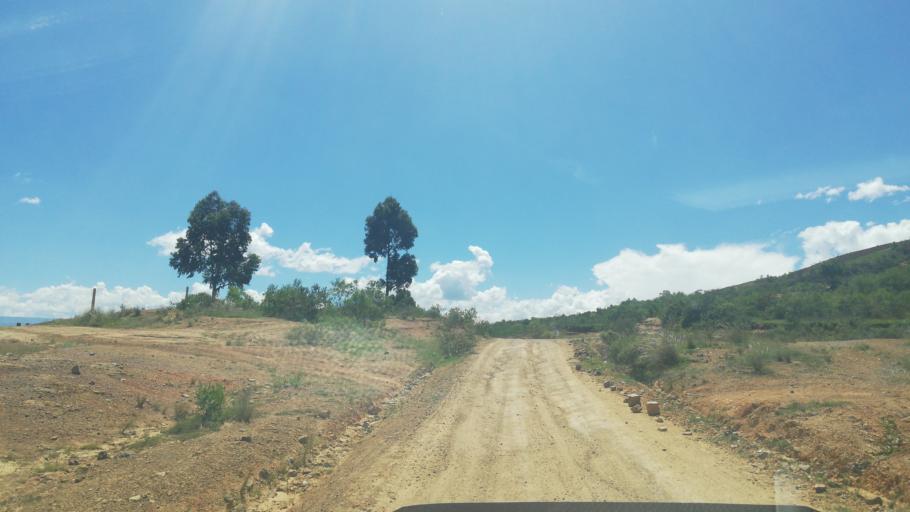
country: BO
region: Cochabamba
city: Totora
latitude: -17.7367
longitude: -65.2224
